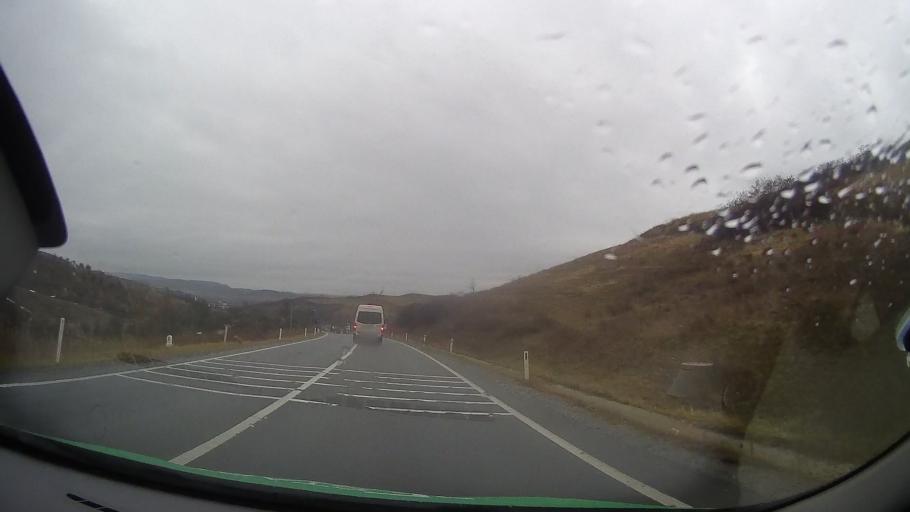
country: RO
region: Bistrita-Nasaud
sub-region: Comuna Galatii Bistritei
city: Galatii Bistritei
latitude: 47.0293
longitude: 24.4197
